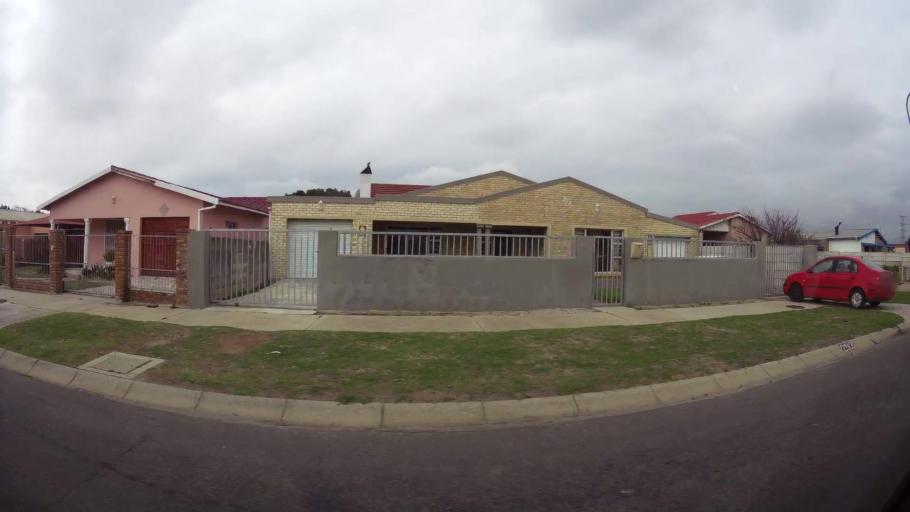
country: ZA
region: Eastern Cape
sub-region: Nelson Mandela Bay Metropolitan Municipality
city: Port Elizabeth
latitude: -33.8990
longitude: 25.5525
